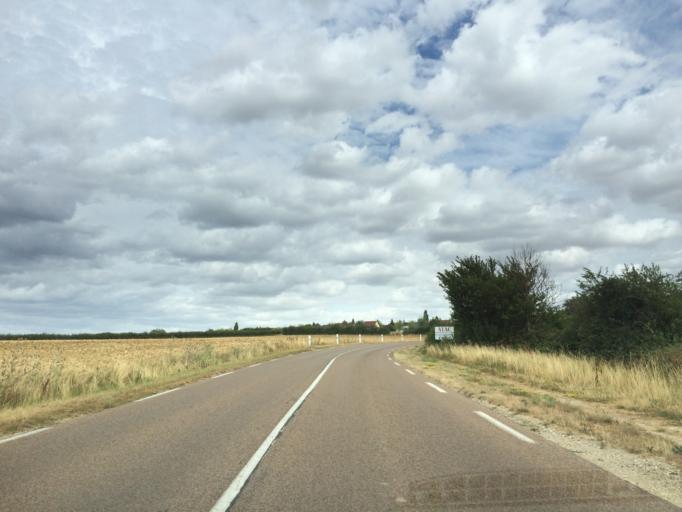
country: FR
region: Bourgogne
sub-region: Departement de l'Yonne
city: Saint-Georges-sur-Baulche
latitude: 47.8003
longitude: 3.5188
